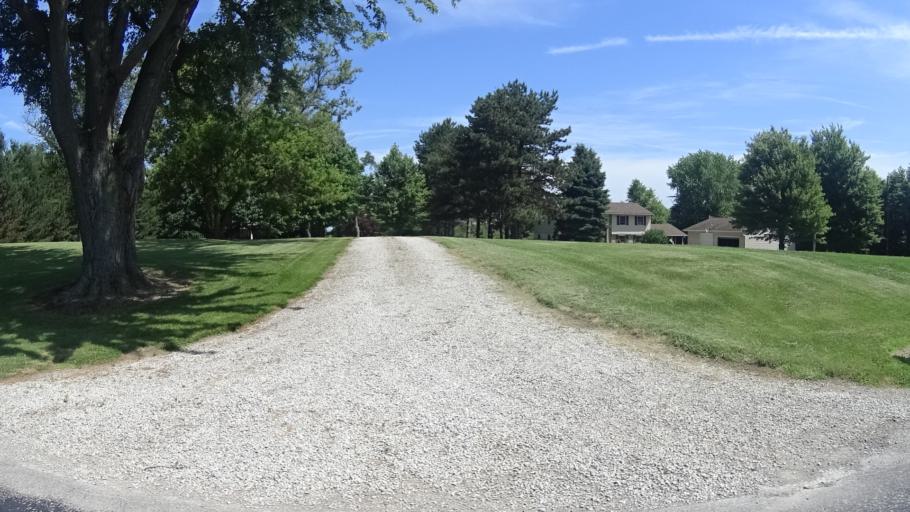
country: US
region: Ohio
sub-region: Lorain County
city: Vermilion
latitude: 41.3542
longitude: -82.4406
